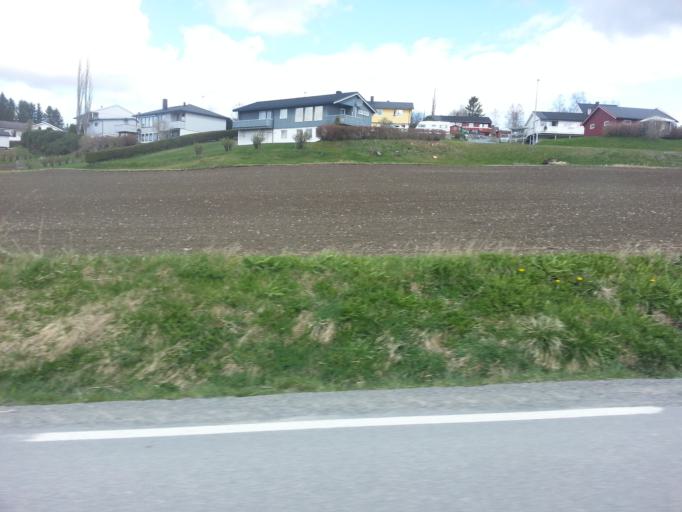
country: NO
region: Nord-Trondelag
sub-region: Levanger
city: Skogn
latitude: 63.6376
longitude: 11.2703
